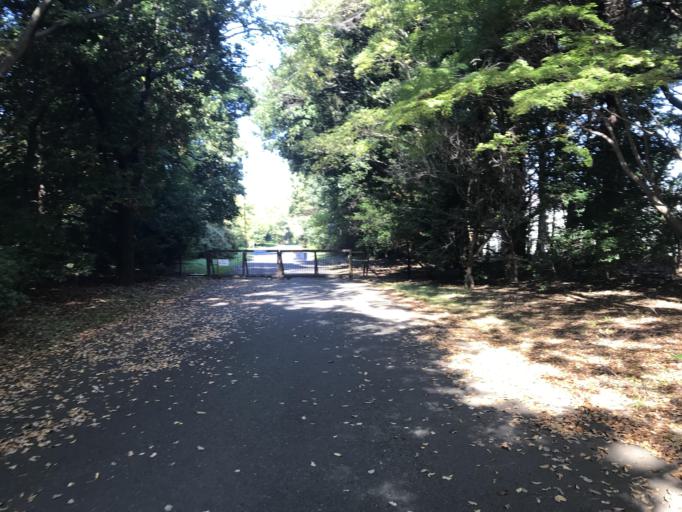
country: JP
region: Tokyo
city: Hino
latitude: 35.7140
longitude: 139.3990
